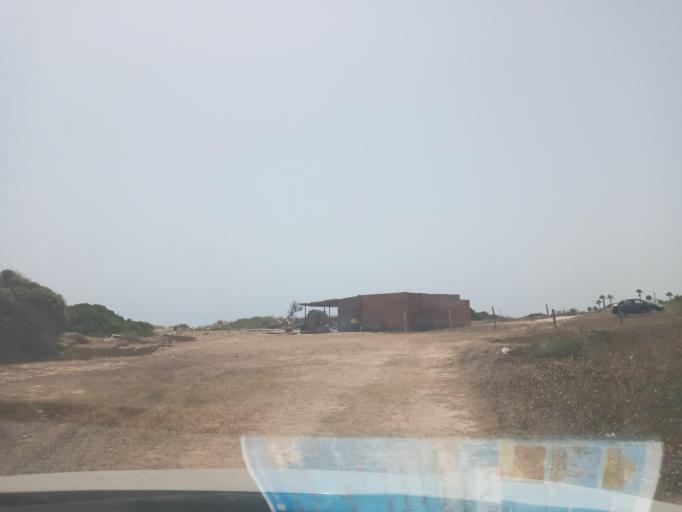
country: TN
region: Nabul
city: El Haouaria
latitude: 37.0255
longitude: 11.0561
